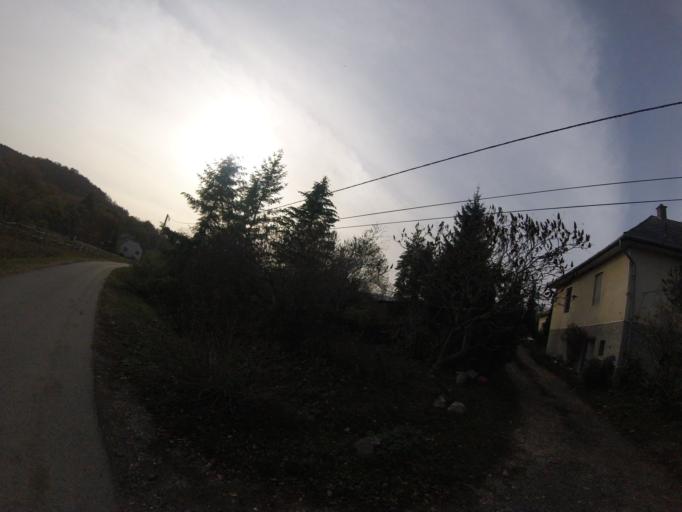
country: HU
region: Borsod-Abauj-Zemplen
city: Gonc
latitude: 48.5150
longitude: 21.4581
